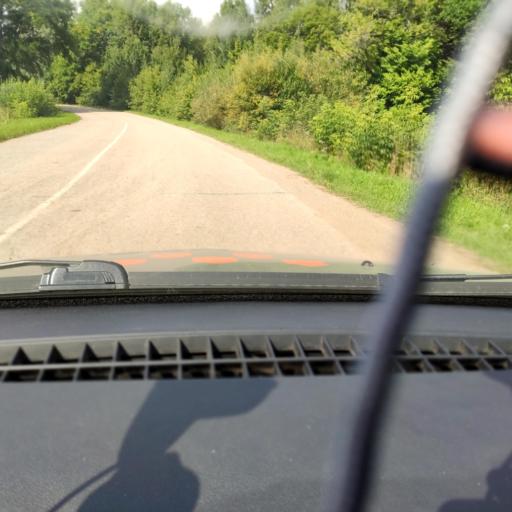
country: RU
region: Bashkortostan
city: Kudeyevskiy
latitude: 54.7306
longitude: 56.6109
